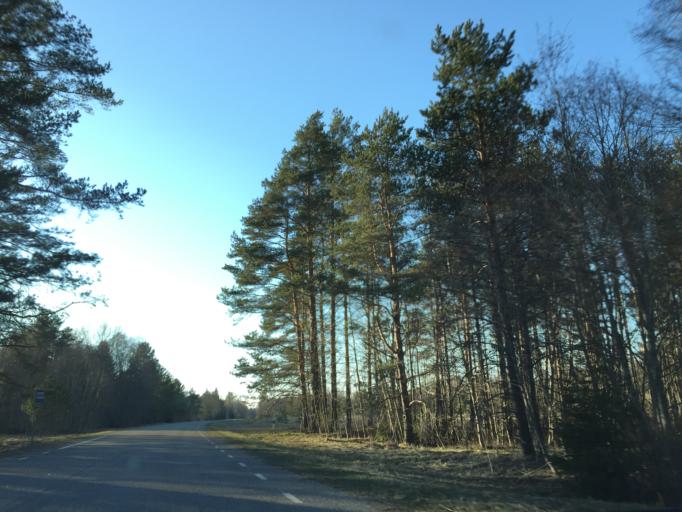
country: EE
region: Ida-Virumaa
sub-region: Sillamaee linn
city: Sillamae
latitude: 59.0850
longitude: 27.6717
